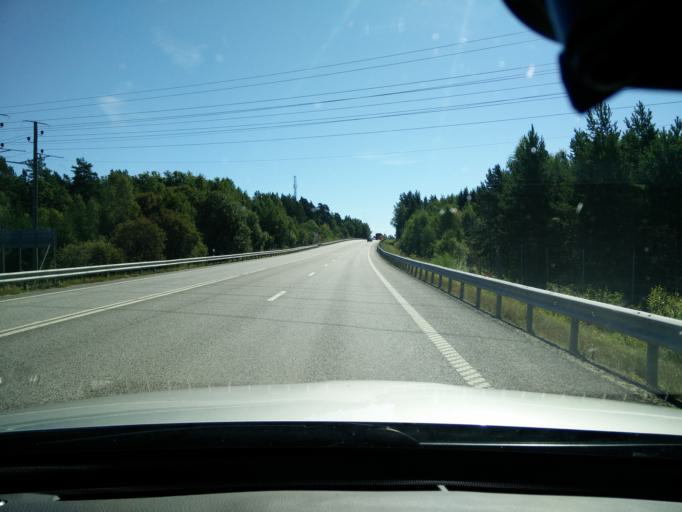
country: SE
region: Stockholm
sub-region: Osterakers Kommun
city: Akersberga
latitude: 59.4520
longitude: 18.2093
